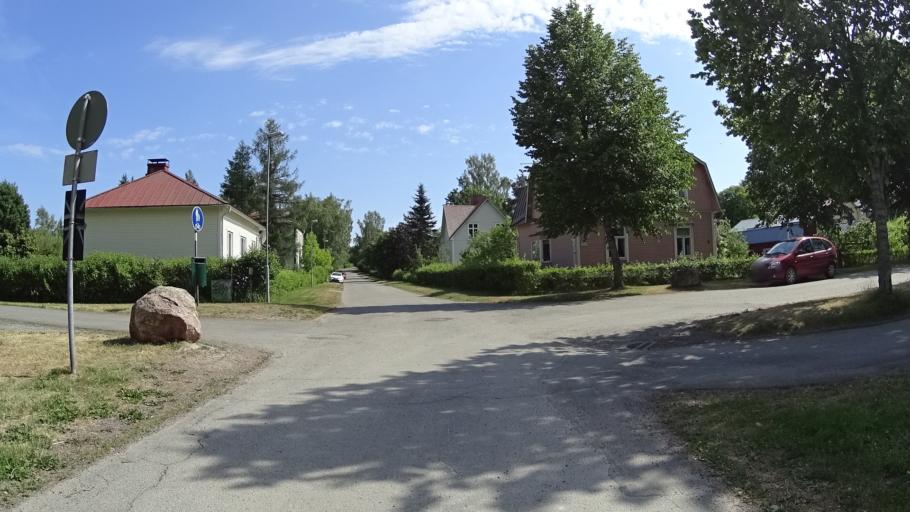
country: FI
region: Uusimaa
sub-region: Raaseporin
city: Karis
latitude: 60.0753
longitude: 23.6667
